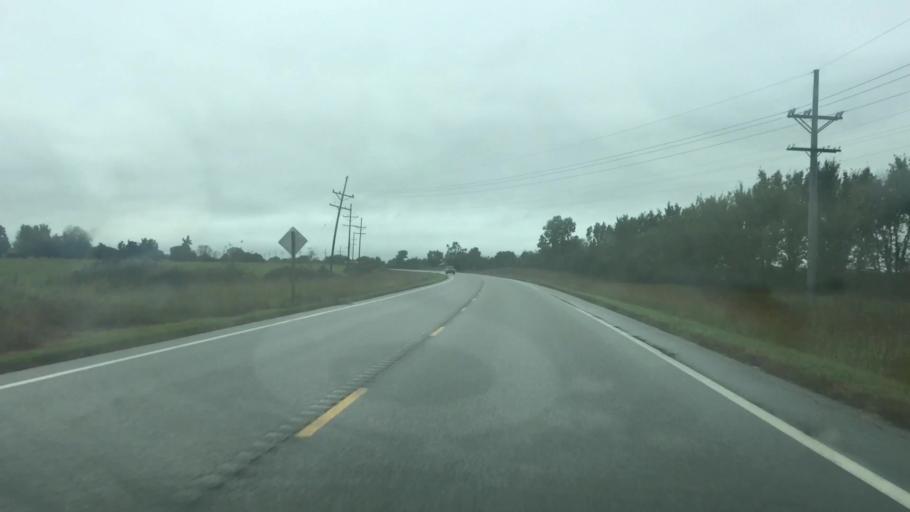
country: US
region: Kansas
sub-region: Anderson County
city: Garnett
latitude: 38.3528
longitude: -95.1558
